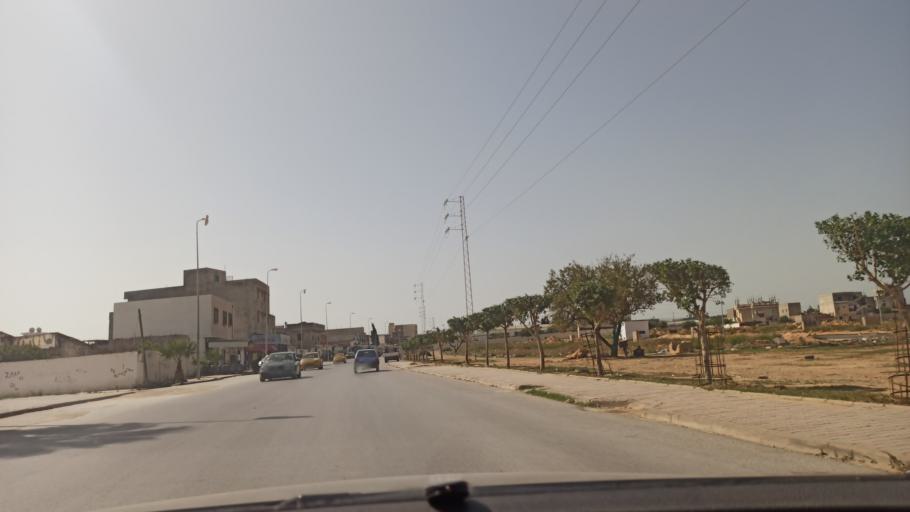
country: TN
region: Manouba
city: Manouba
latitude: 36.7640
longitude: 10.1099
